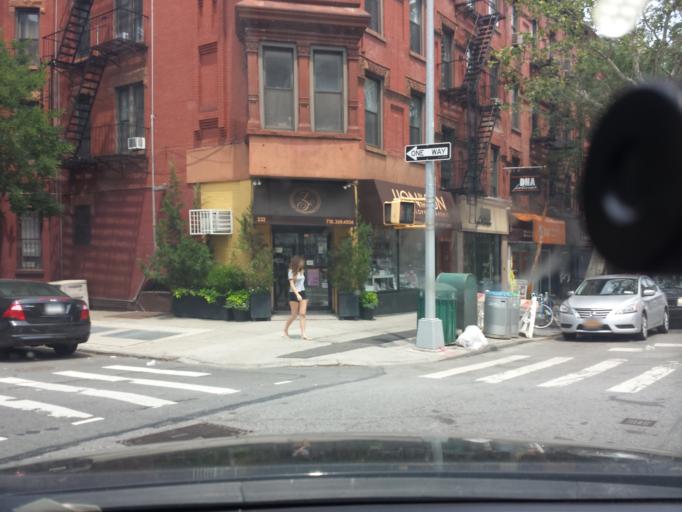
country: US
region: New York
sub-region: Kings County
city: Brooklyn
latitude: 40.6698
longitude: -73.9790
